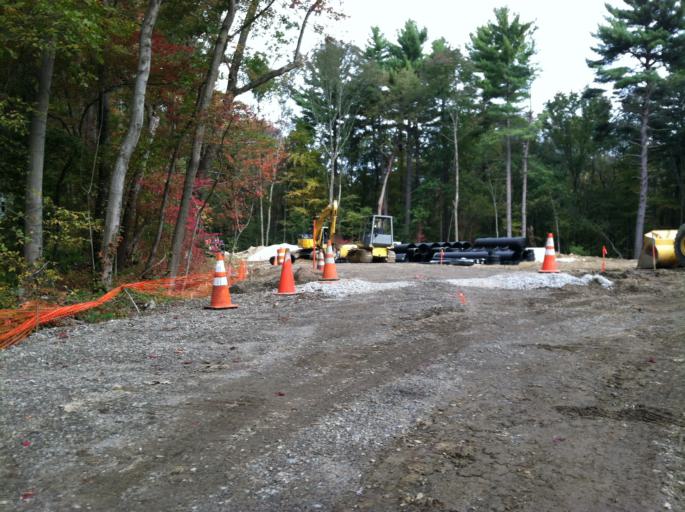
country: US
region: Massachusetts
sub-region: Middlesex County
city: Bedford
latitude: 42.5018
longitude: -71.2777
